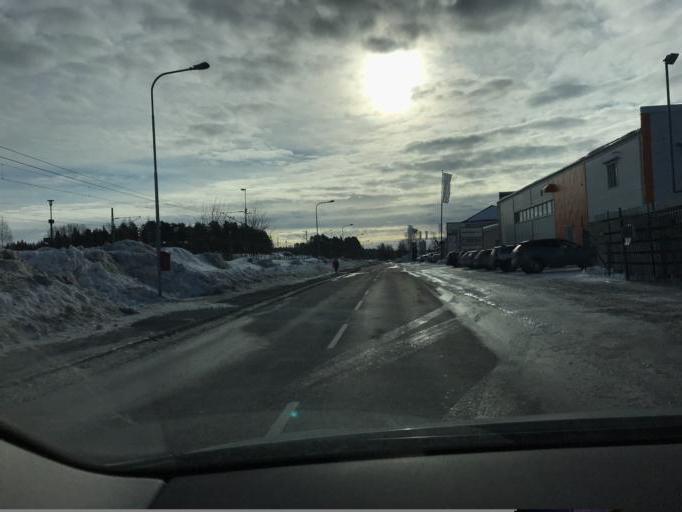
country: SE
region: Norrbotten
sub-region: Lulea Kommun
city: Bergnaset
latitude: 65.6104
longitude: 22.1188
